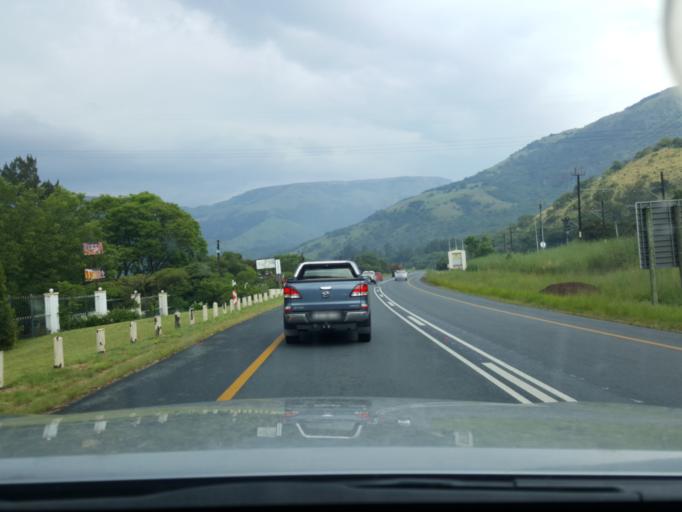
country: ZA
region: Mpumalanga
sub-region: Nkangala District Municipality
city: Belfast
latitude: -25.6452
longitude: 30.3735
